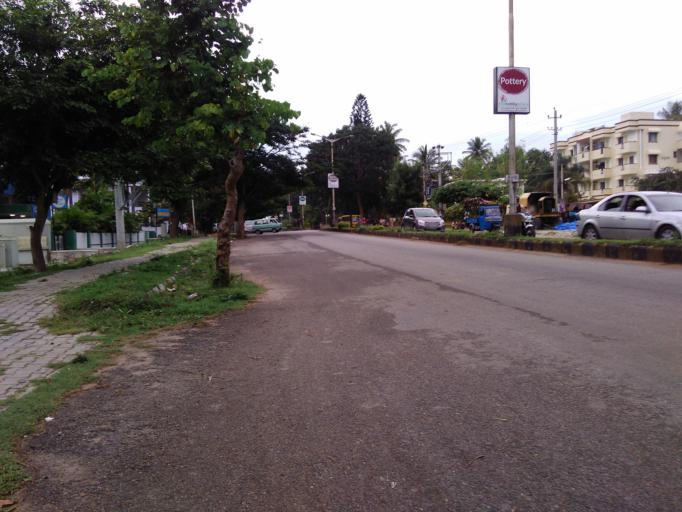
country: IN
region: Karnataka
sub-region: Mysore
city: Mysore
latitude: 12.3203
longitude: 76.6271
